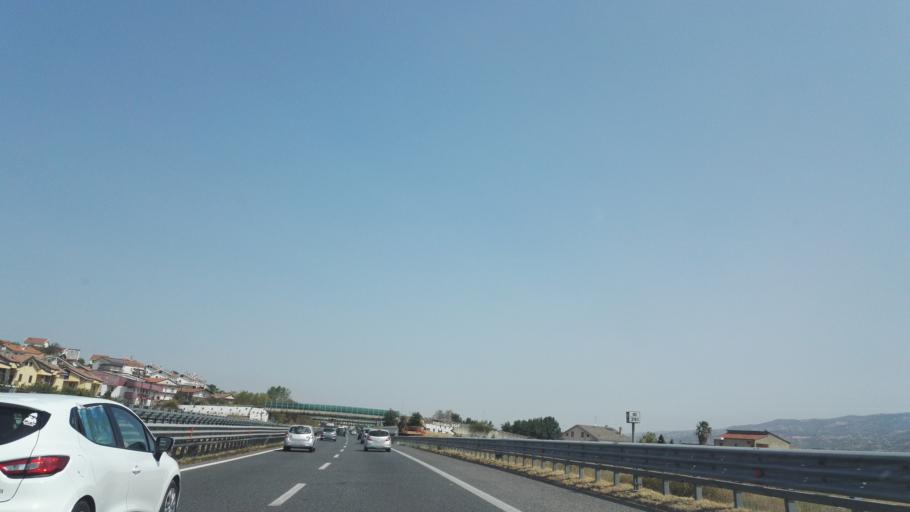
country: IT
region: Calabria
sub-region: Provincia di Cosenza
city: Settimo
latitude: 39.3686
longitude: 16.2366
